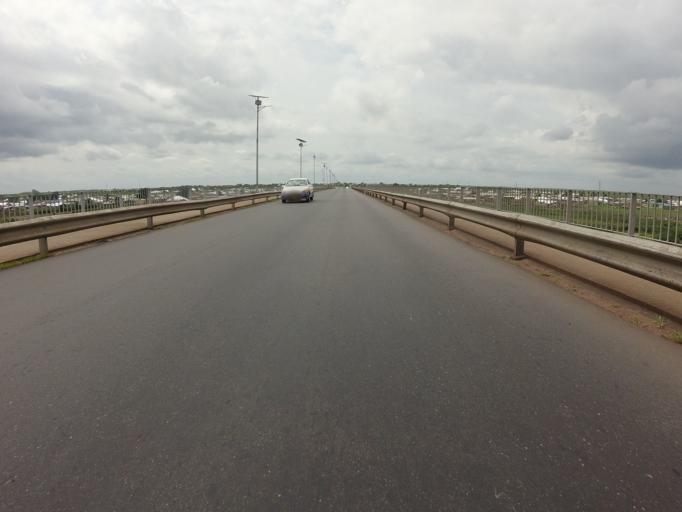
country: GH
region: Brong-Ahafo
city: Kintampo
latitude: 8.7659
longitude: -1.4546
